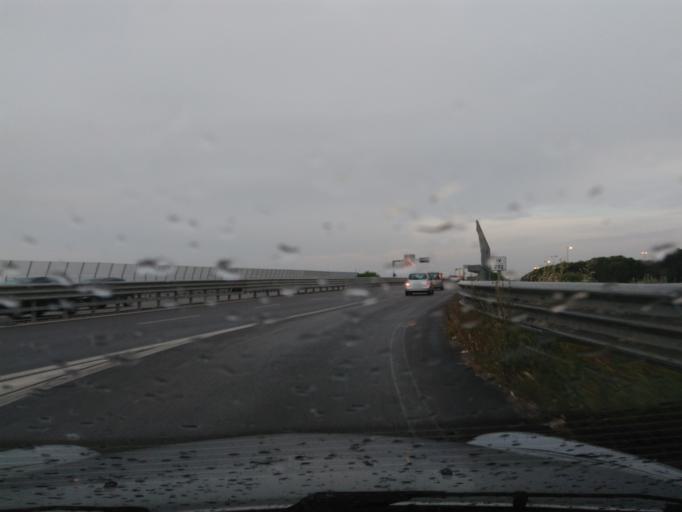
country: IT
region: Apulia
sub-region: Provincia di Bari
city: Molfetta
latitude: 41.2071
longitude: 16.5603
